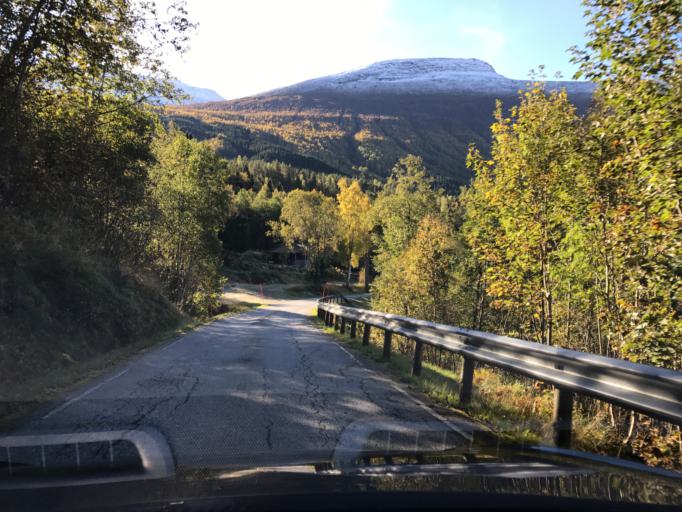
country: NO
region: More og Romsdal
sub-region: Norddal
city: Valldal
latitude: 62.3327
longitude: 7.3895
